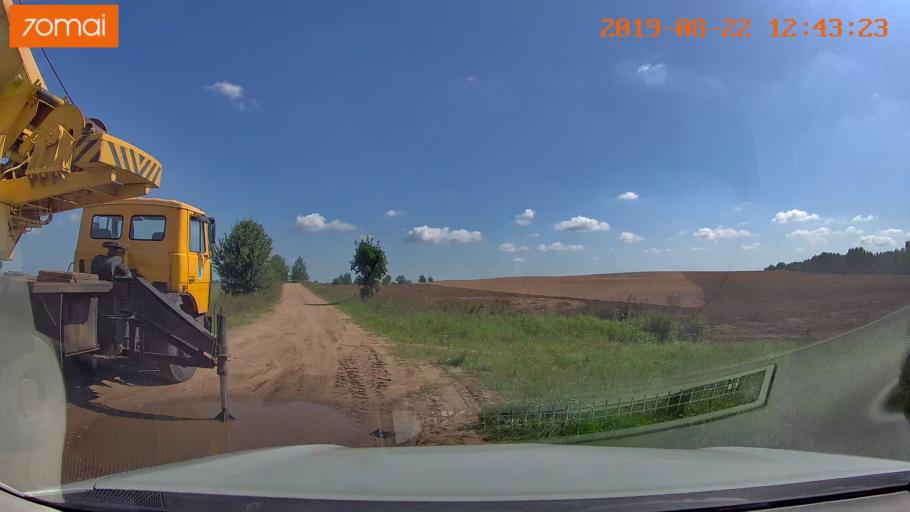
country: BY
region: Minsk
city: Prawdzinski
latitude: 53.4505
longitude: 27.5986
